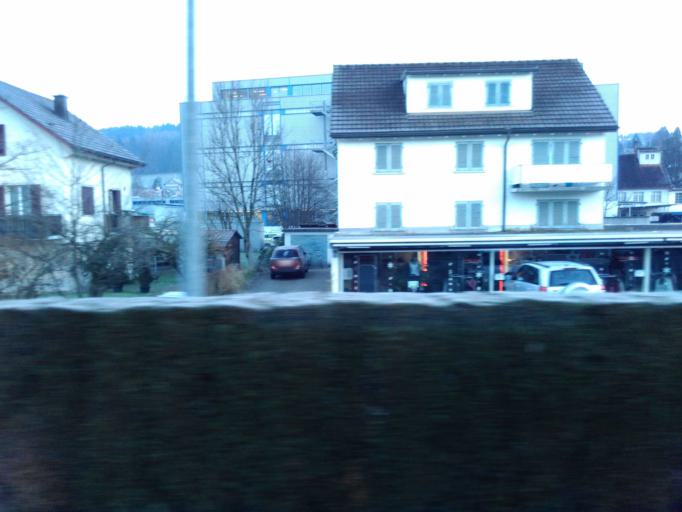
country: CH
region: Saint Gallen
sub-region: Wahlkreis See-Gaster
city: Uznach
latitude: 47.2247
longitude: 8.9798
